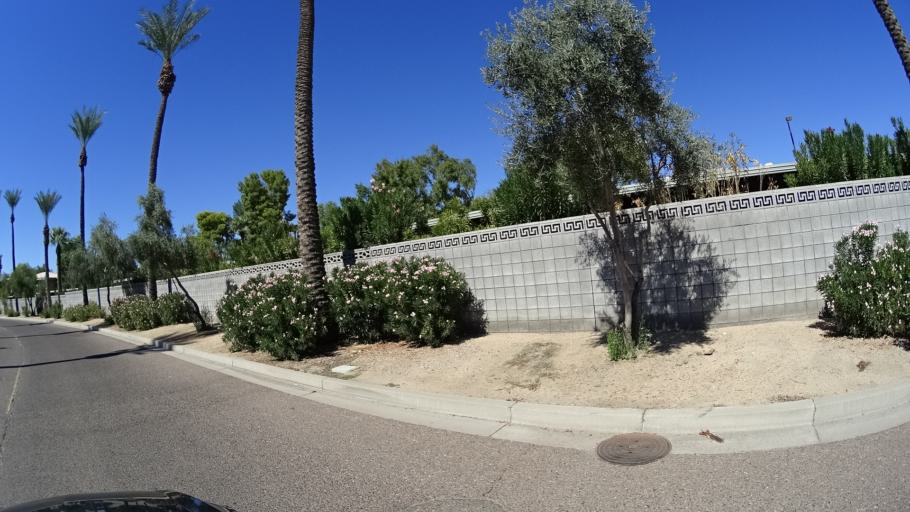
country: US
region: Arizona
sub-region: Maricopa County
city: Phoenix
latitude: 33.5117
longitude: -112.0259
